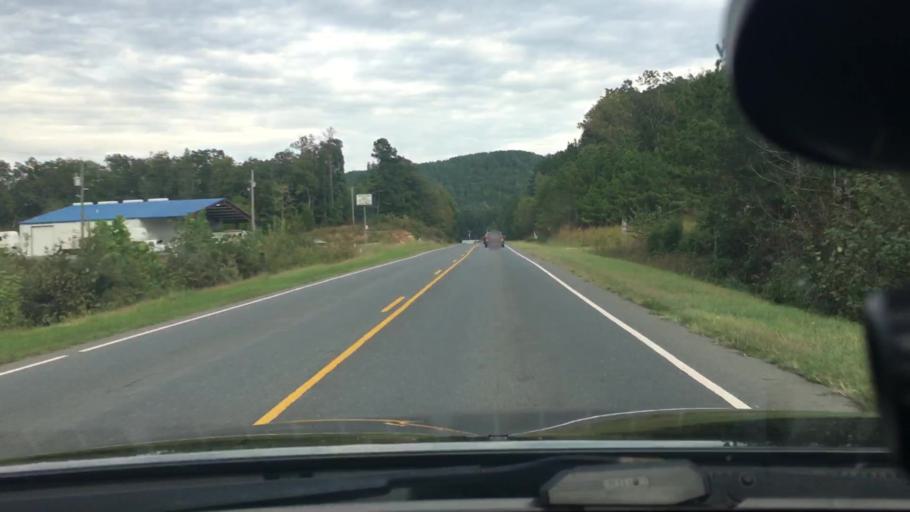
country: US
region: North Carolina
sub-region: Stanly County
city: Norwood
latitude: 35.3066
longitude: -80.0661
